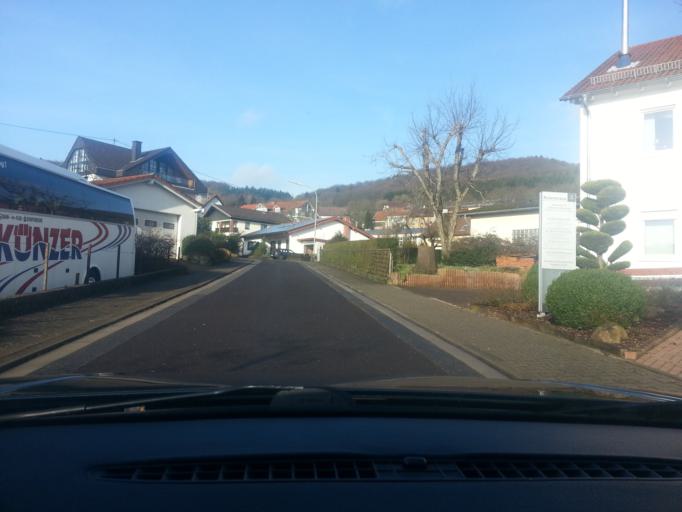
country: DE
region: Rheinland-Pfalz
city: Reichweiler
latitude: 49.5239
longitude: 7.2587
